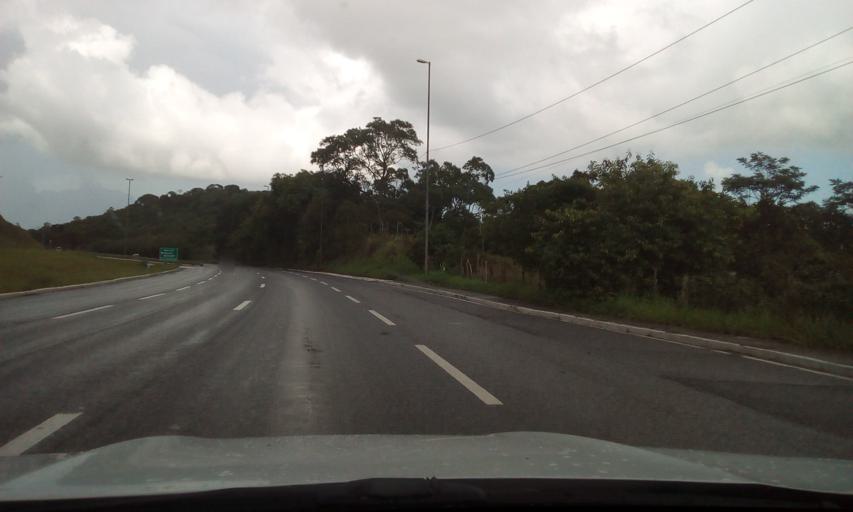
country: BR
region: Pernambuco
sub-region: Cabo De Santo Agostinho
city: Cabo
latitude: -8.3079
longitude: -35.0769
